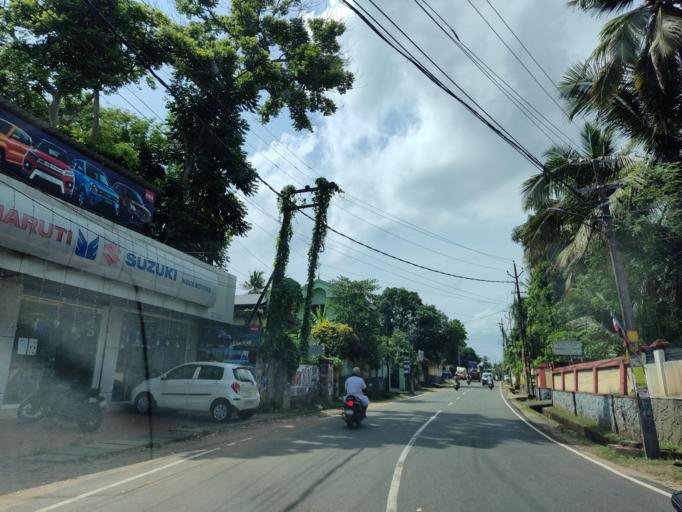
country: IN
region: Kerala
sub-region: Alappuzha
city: Mavelikara
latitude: 9.2556
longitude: 76.5449
